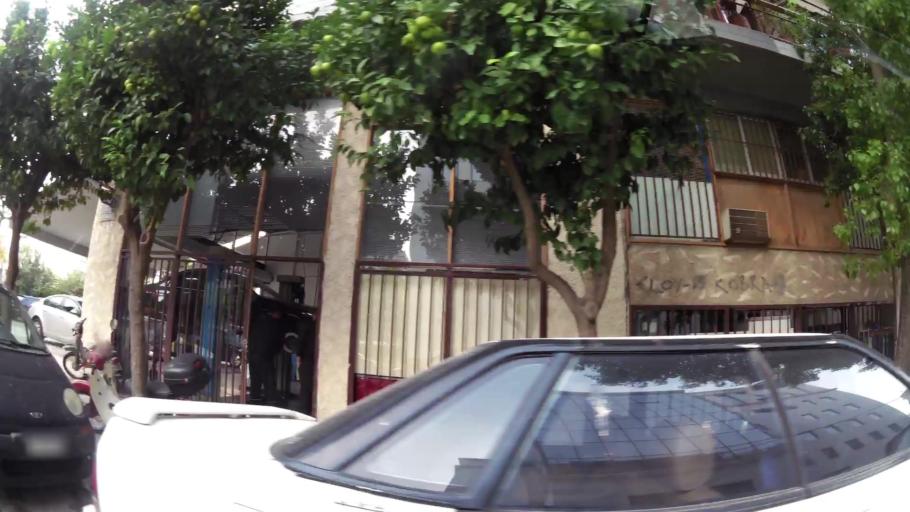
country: GR
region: Attica
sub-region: Nomarchia Athinas
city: Kallithea
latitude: 37.9448
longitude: 23.6980
